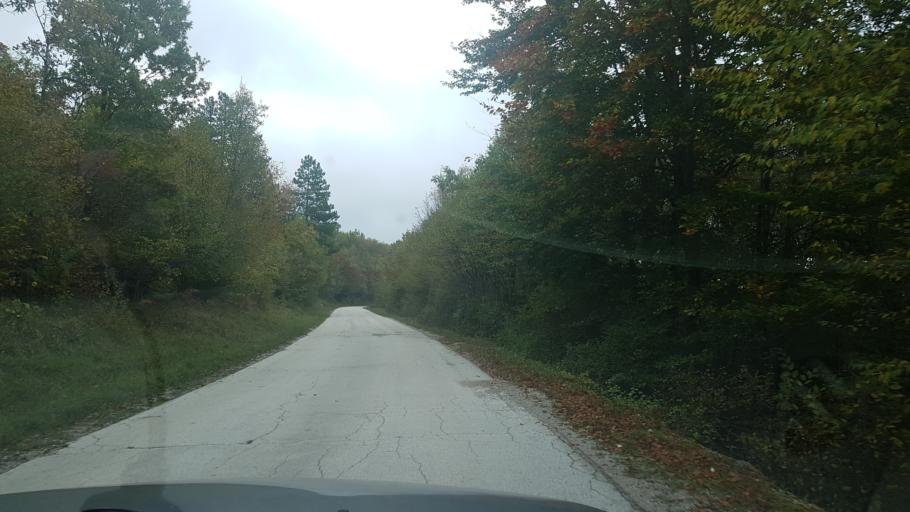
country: HR
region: Istarska
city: Buzet
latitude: 45.5070
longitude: 13.9723
